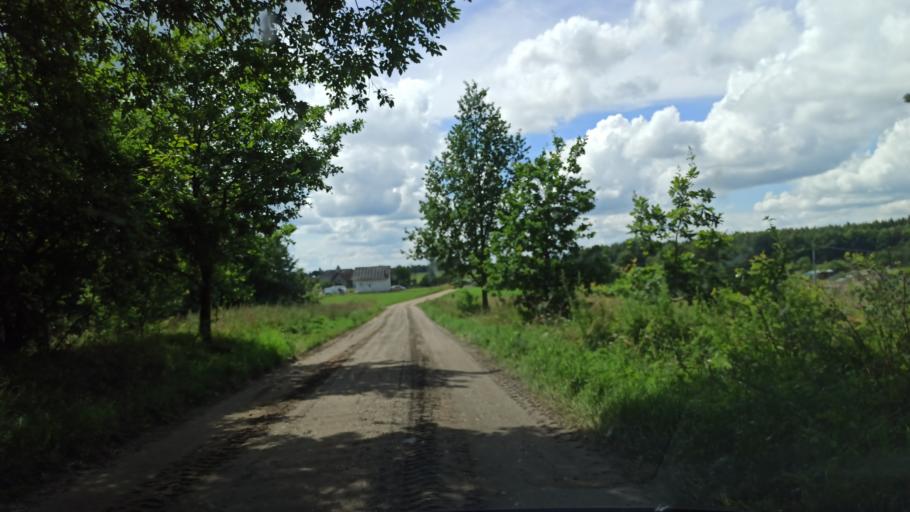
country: PL
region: Warmian-Masurian Voivodeship
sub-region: Powiat ostrodzki
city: Morag
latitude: 53.8654
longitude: 20.0415
